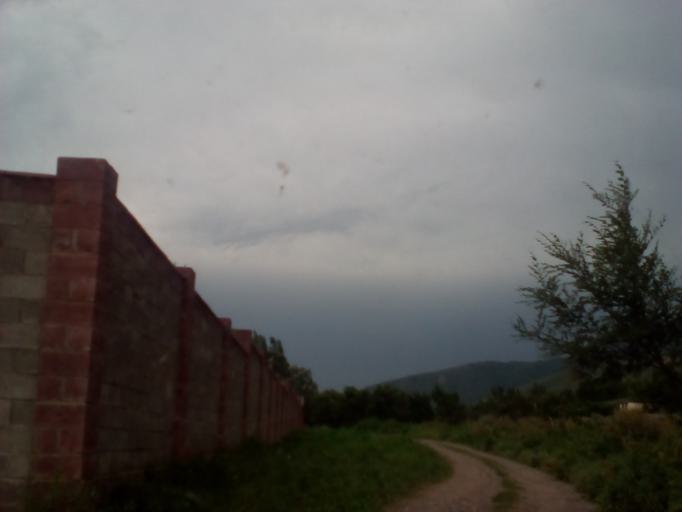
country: KZ
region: Almaty Oblysy
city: Burunday
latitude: 43.1579
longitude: 76.3988
